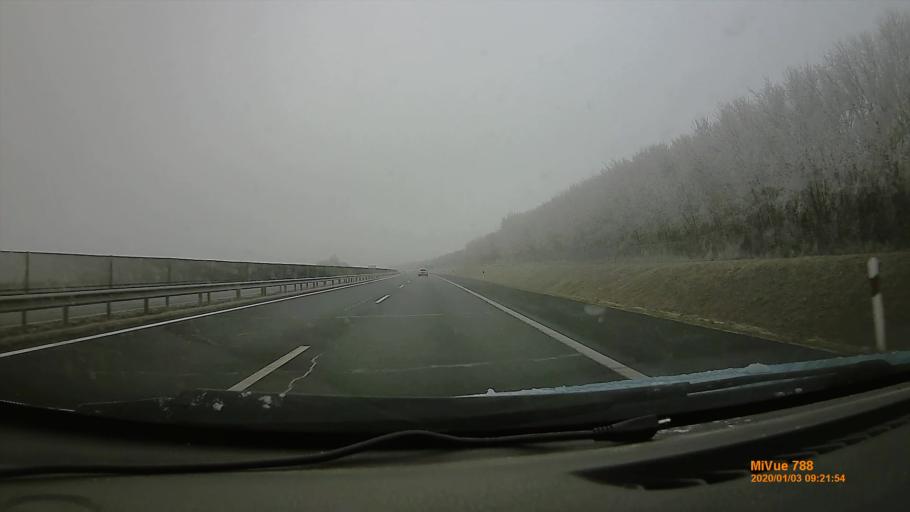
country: HU
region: Fejer
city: Ivancsa
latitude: 47.1429
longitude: 18.8086
